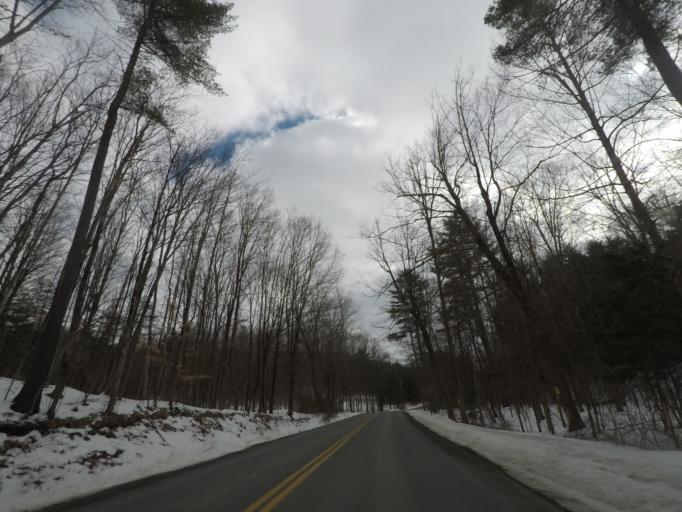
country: US
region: New York
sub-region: Rensselaer County
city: Hoosick Falls
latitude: 42.8909
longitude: -73.4202
